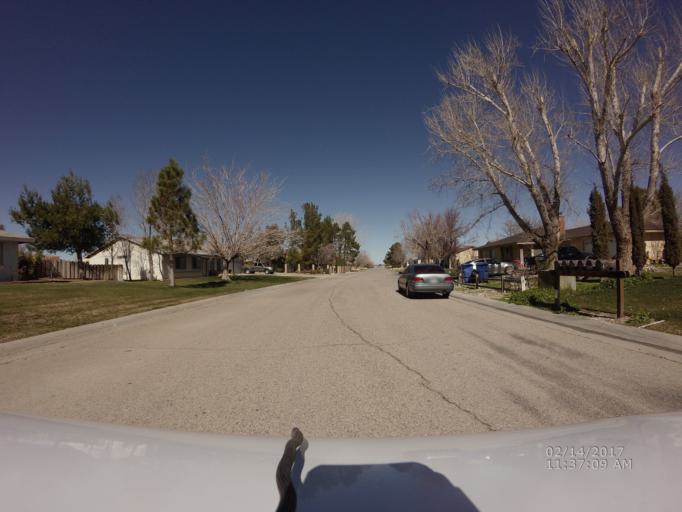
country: US
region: California
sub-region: Los Angeles County
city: Littlerock
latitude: 34.5618
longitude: -117.9559
